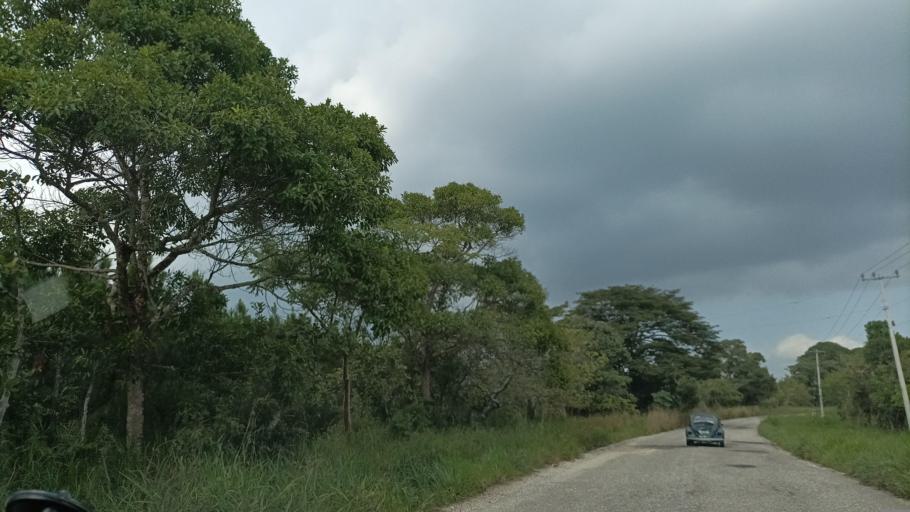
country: MX
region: Veracruz
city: Las Choapas
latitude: 17.8226
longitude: -94.1091
